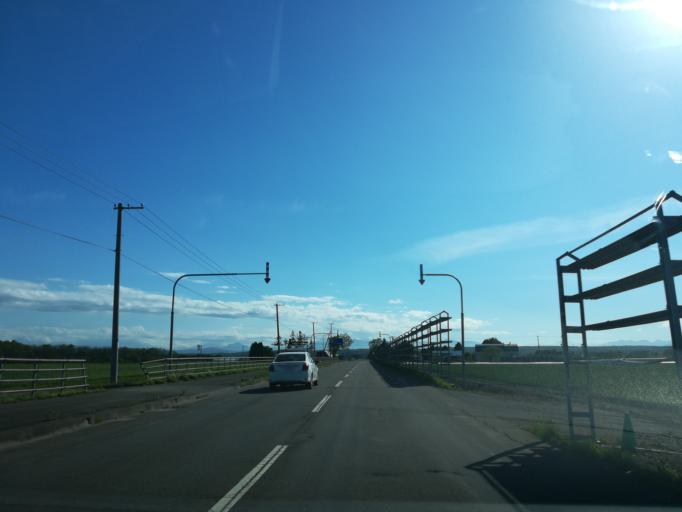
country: JP
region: Hokkaido
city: Kitahiroshima
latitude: 43.0416
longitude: 141.5863
